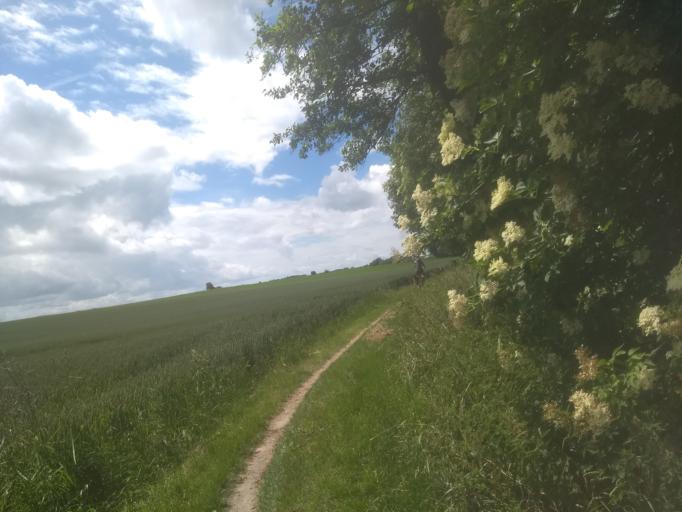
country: FR
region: Nord-Pas-de-Calais
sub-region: Departement du Pas-de-Calais
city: Agny
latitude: 50.2529
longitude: 2.7363
